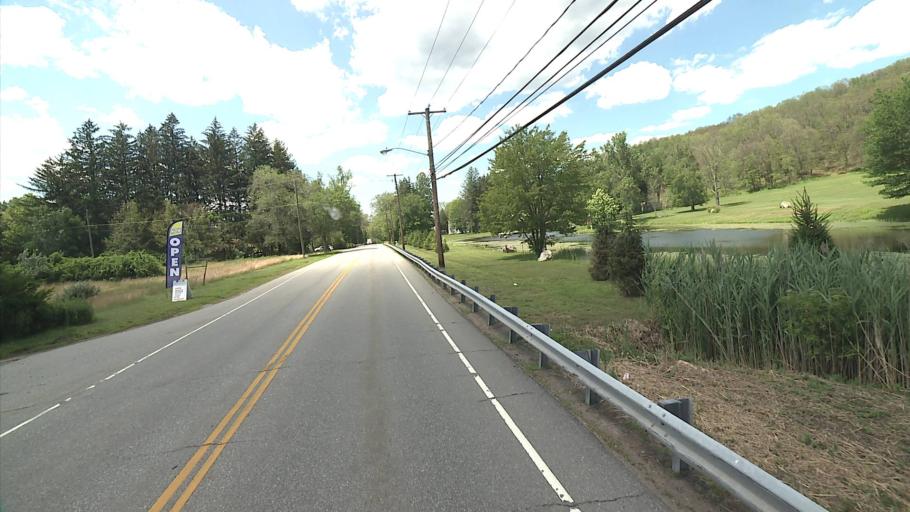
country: US
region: Connecticut
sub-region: Middlesex County
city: Moodus
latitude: 41.5053
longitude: -72.4764
